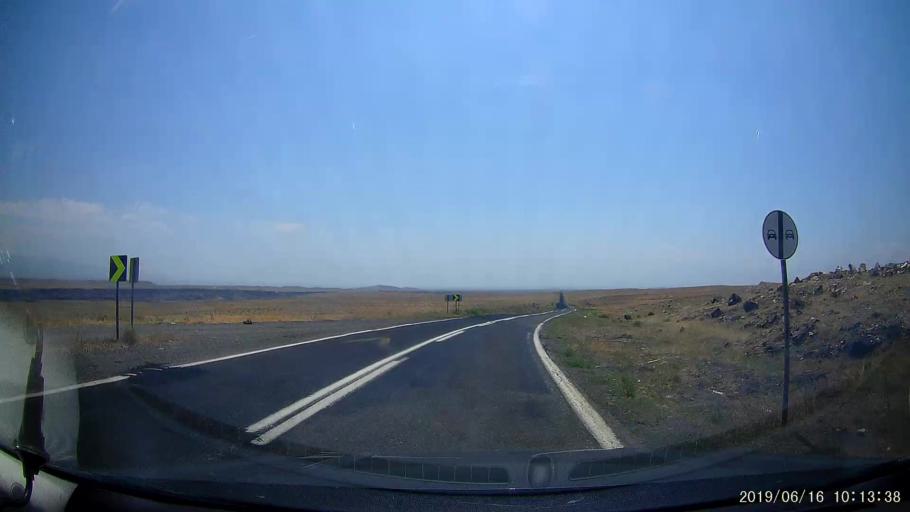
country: TR
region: Igdir
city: Tuzluca
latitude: 40.1917
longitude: 43.6465
